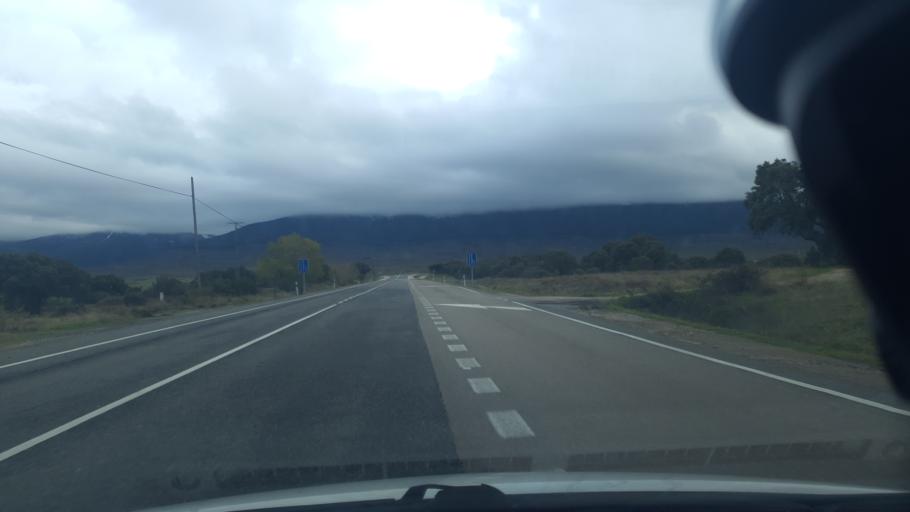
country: ES
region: Castille and Leon
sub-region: Provincia de Segovia
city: Cerezo de Abajo
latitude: 41.2133
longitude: -3.5852
